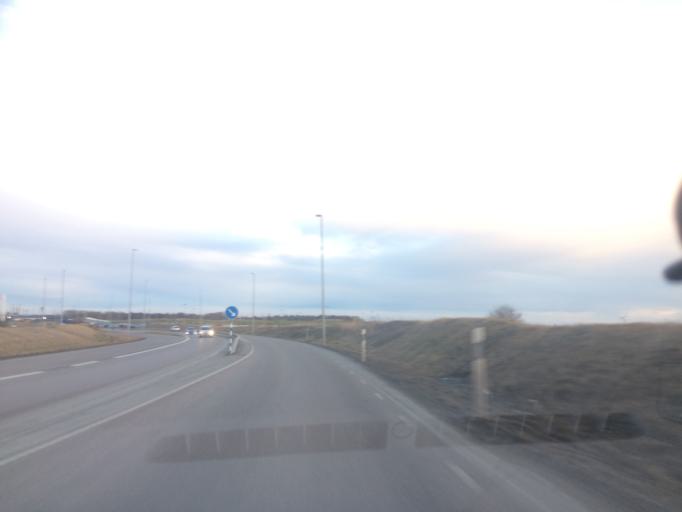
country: SE
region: Vaestra Goetaland
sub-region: Goteborg
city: Torslanda
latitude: 57.7085
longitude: 11.7731
